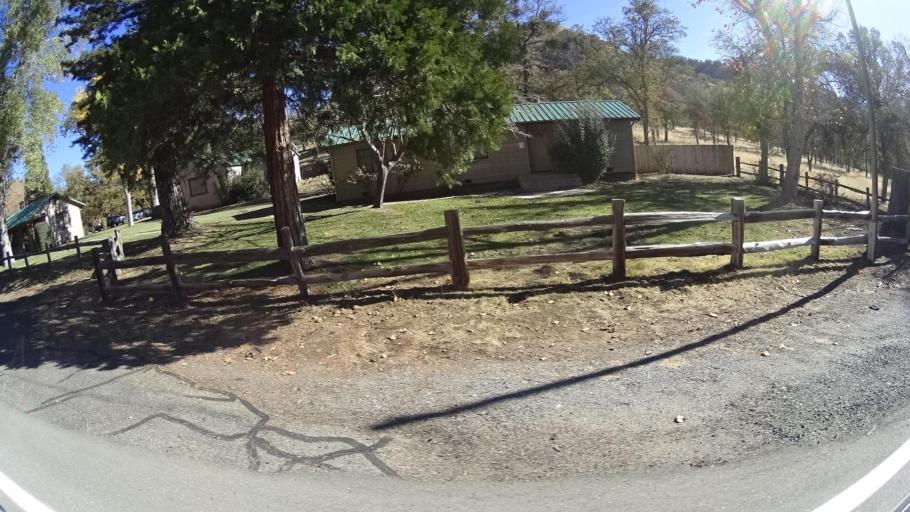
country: US
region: California
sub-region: Kern County
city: Alta Sierra
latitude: 35.7241
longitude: -118.6803
